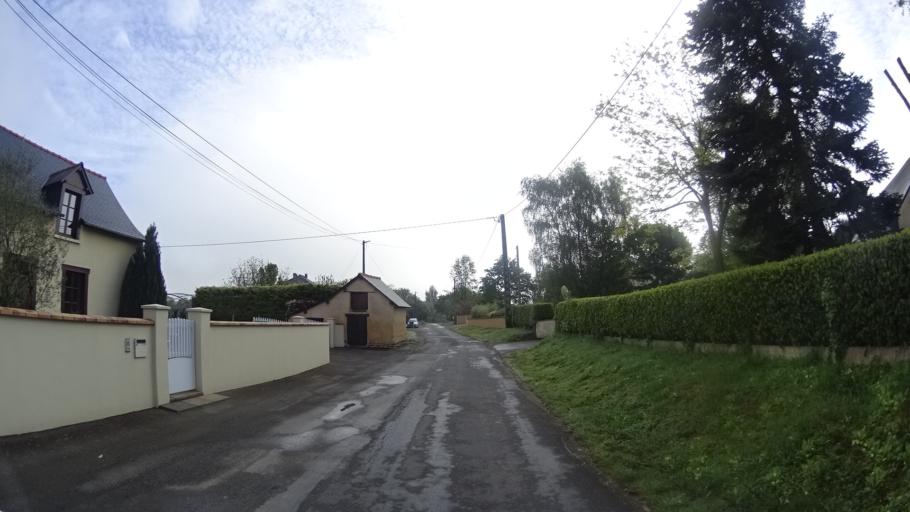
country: FR
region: Brittany
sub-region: Departement d'Ille-et-Vilaine
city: Mordelles
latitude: 48.0835
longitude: -1.8330
